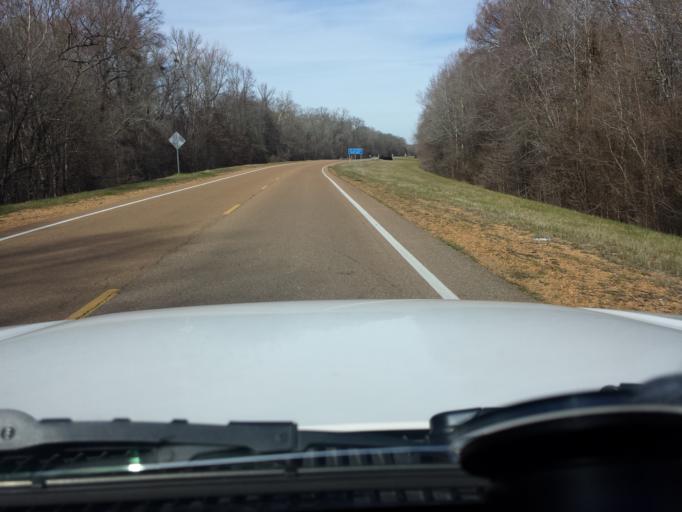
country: US
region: Mississippi
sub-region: Madison County
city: Canton
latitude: 32.7115
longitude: -90.0959
